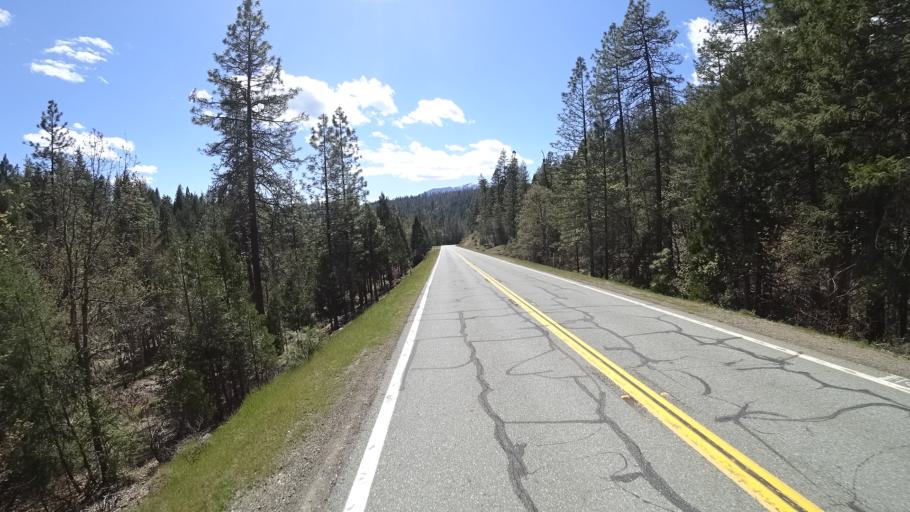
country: US
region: California
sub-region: Trinity County
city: Lewiston
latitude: 40.8658
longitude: -122.8053
